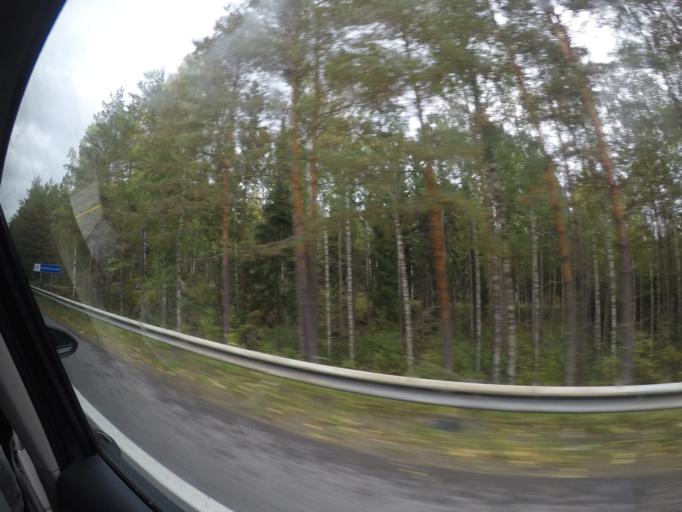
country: FI
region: Haeme
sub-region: Haemeenlinna
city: Parola
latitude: 61.1648
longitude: 24.4109
